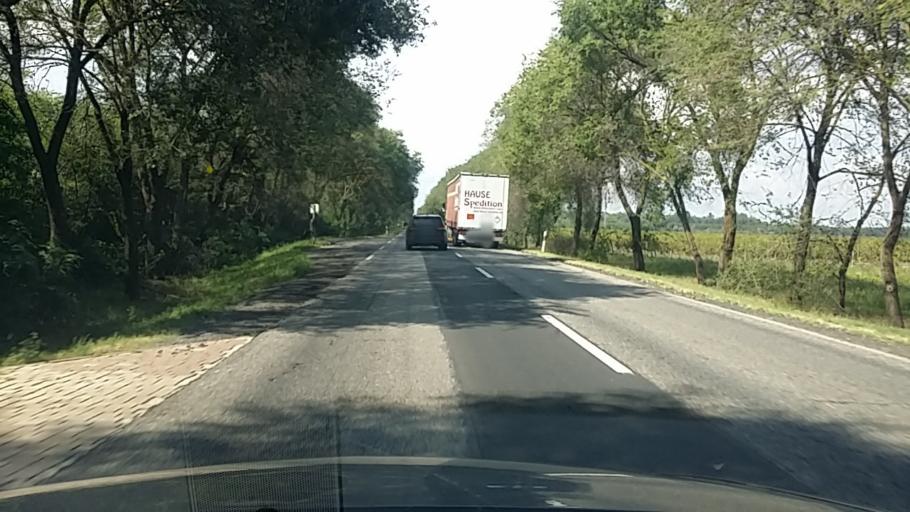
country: HU
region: Bacs-Kiskun
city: Nyarlorinc
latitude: 46.8945
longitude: 19.8273
